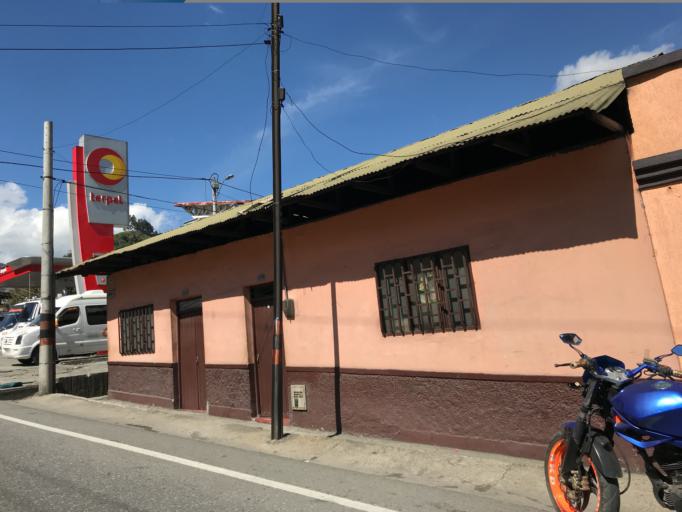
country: CO
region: Tolima
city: Cajamarca
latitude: 4.4406
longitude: -75.4310
